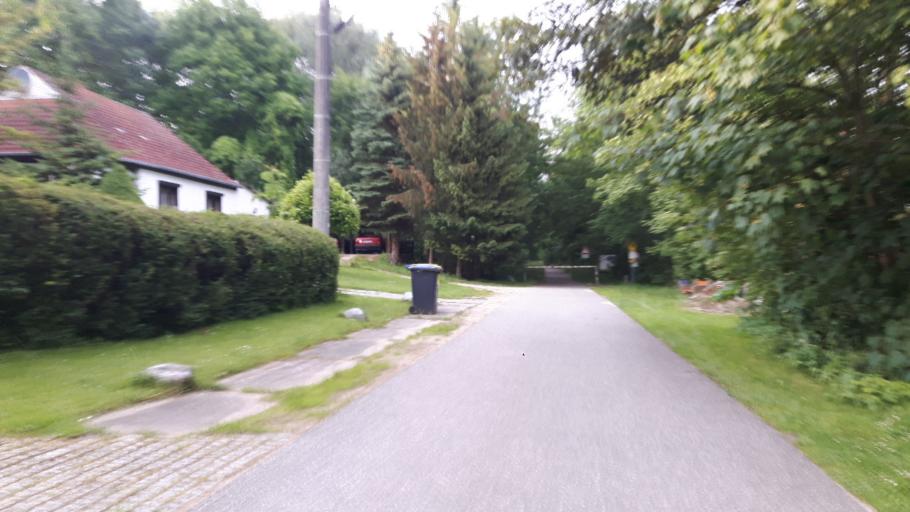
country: DE
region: Brandenburg
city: Gartz
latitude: 53.2125
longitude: 14.4020
